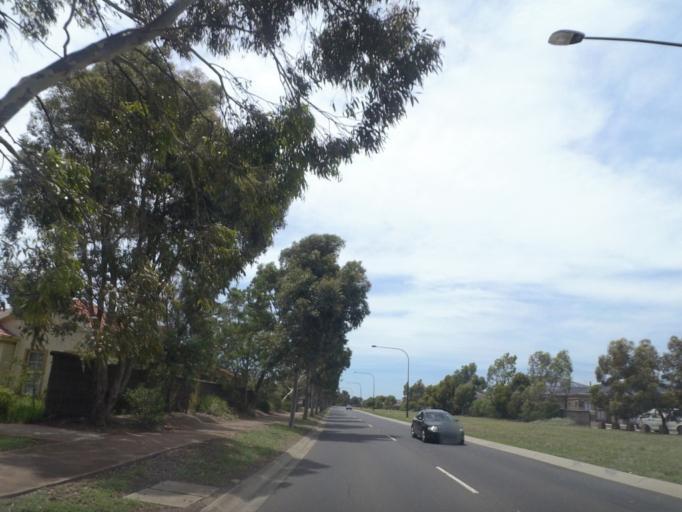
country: AU
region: Victoria
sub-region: Melton
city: Caroline Springs
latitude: -37.7443
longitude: 144.7290
